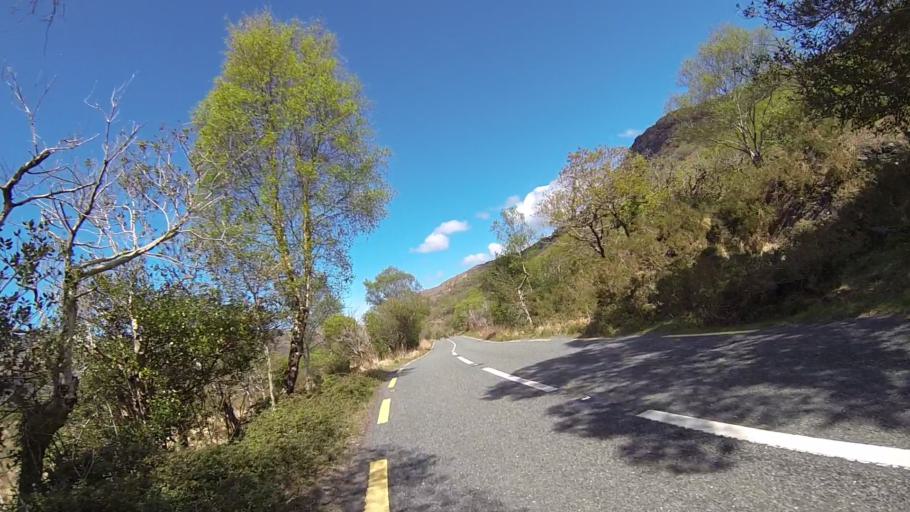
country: IE
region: Munster
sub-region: Ciarrai
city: Kenmare
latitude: 51.9737
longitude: -9.5800
